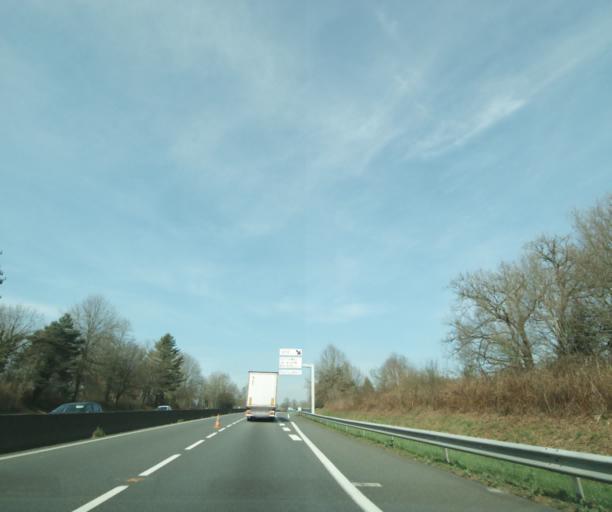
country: FR
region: Limousin
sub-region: Departement de la Haute-Vienne
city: Boisseuil
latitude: 45.7514
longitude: 1.3355
